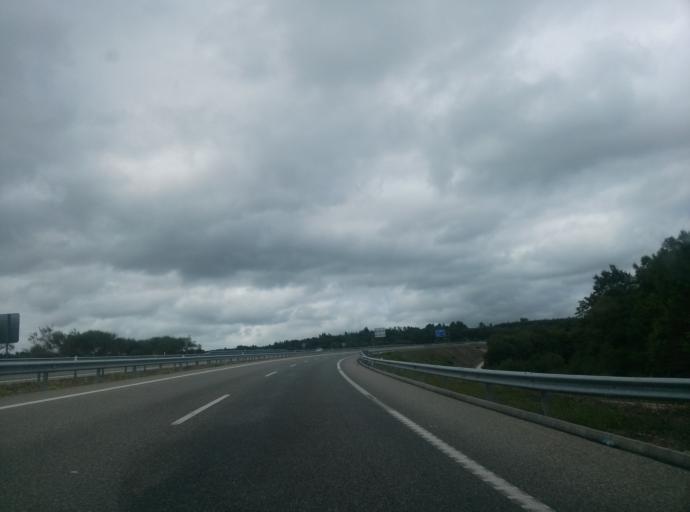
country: ES
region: Galicia
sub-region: Provincia de Lugo
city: Vilalba
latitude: 43.3093
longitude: -7.7060
